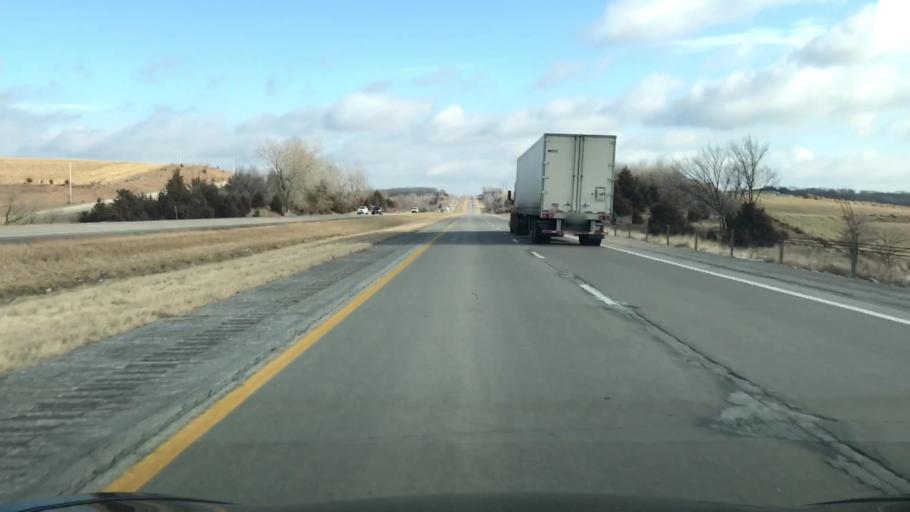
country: US
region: Iowa
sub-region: Cass County
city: Atlantic
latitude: 41.4971
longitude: -94.9094
